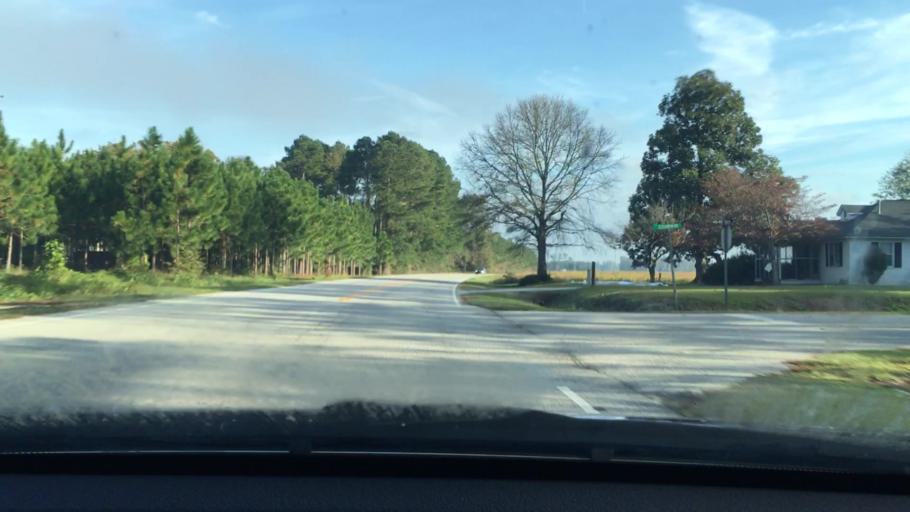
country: US
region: South Carolina
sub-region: Sumter County
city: East Sumter
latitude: 34.0073
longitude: -80.2870
